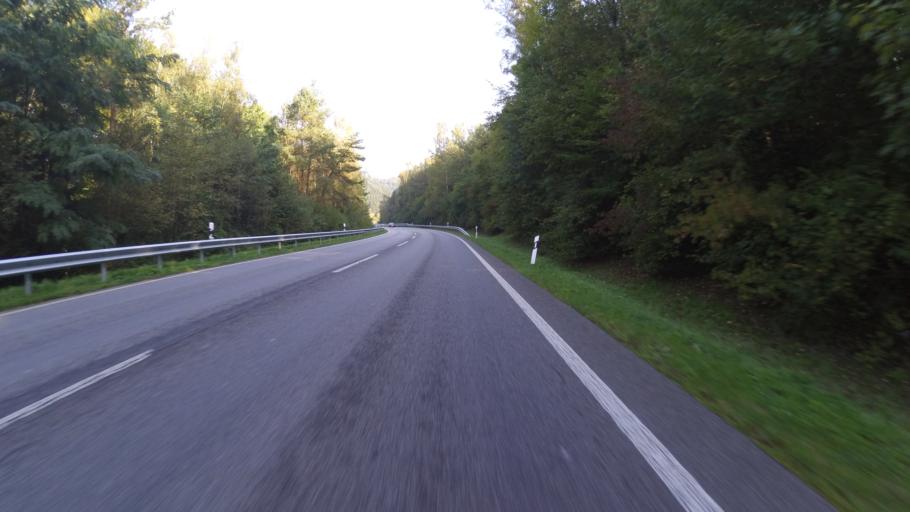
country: DE
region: Rheinland-Pfalz
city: Donsieders
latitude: 49.2629
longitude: 7.5940
